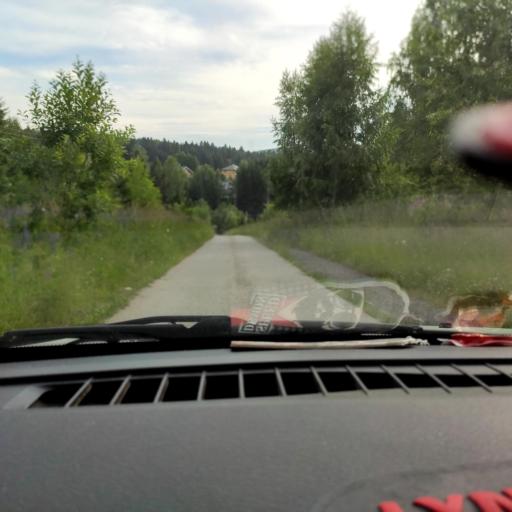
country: RU
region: Perm
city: Polazna
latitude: 58.2524
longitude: 56.2571
